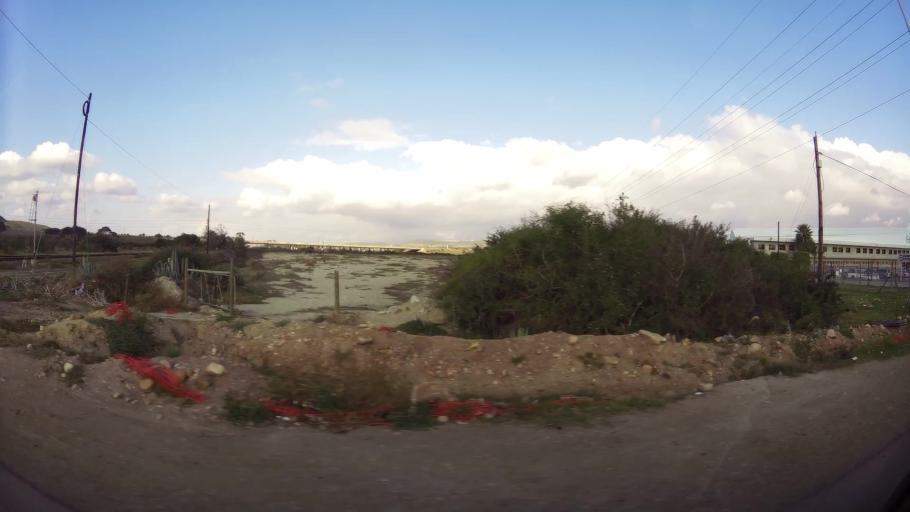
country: ZA
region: Eastern Cape
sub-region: Nelson Mandela Bay Metropolitan Municipality
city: Uitenhage
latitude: -33.7841
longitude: 25.4269
